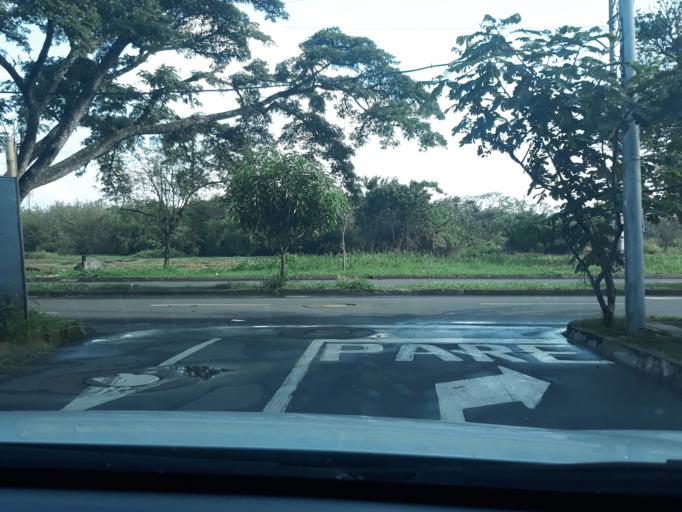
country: CO
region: Valle del Cauca
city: Cali
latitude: 3.3557
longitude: -76.5219
